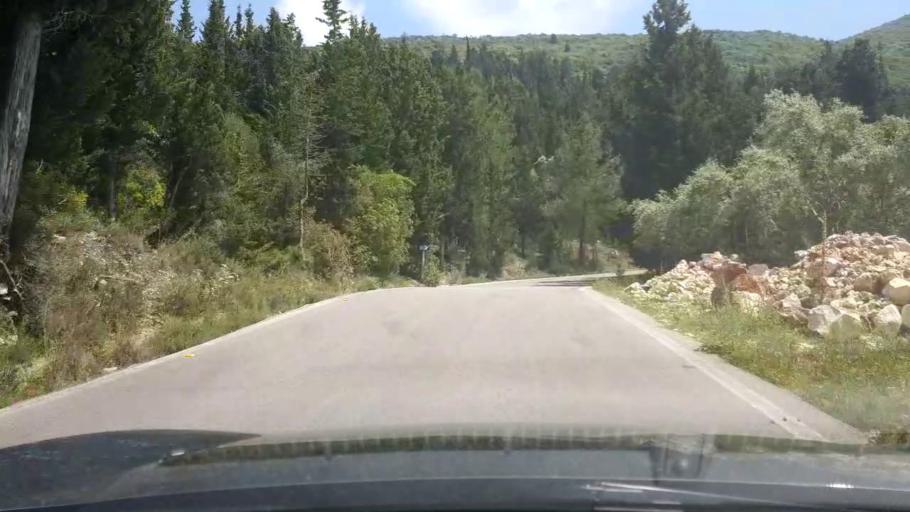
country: GR
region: Ionian Islands
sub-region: Lefkada
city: Nidri
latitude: 38.6526
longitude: 20.7078
